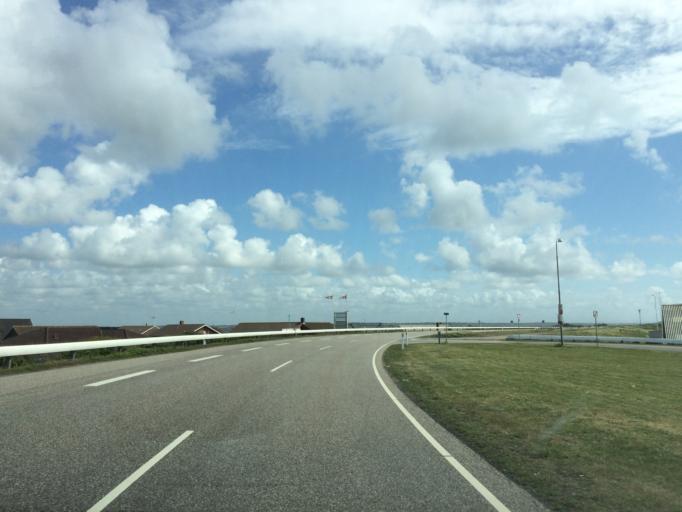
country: DK
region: Central Jutland
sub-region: Holstebro Kommune
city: Ulfborg
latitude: 56.3692
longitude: 8.1220
